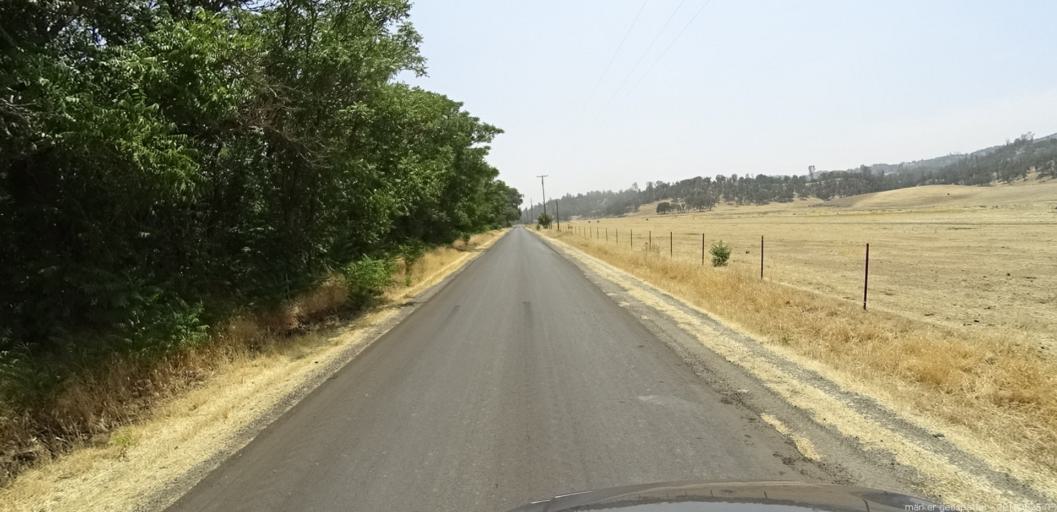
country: US
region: California
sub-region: Fresno County
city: Coalinga
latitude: 35.9513
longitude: -120.4746
